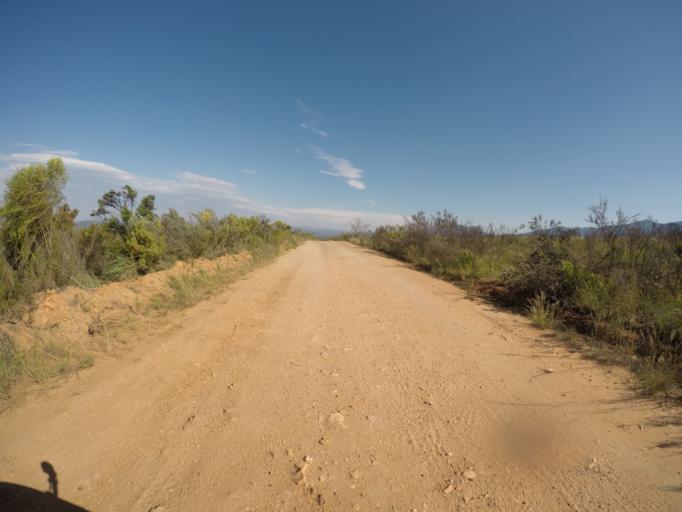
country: ZA
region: Eastern Cape
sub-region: Cacadu District Municipality
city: Kareedouw
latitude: -33.6350
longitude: 24.4698
